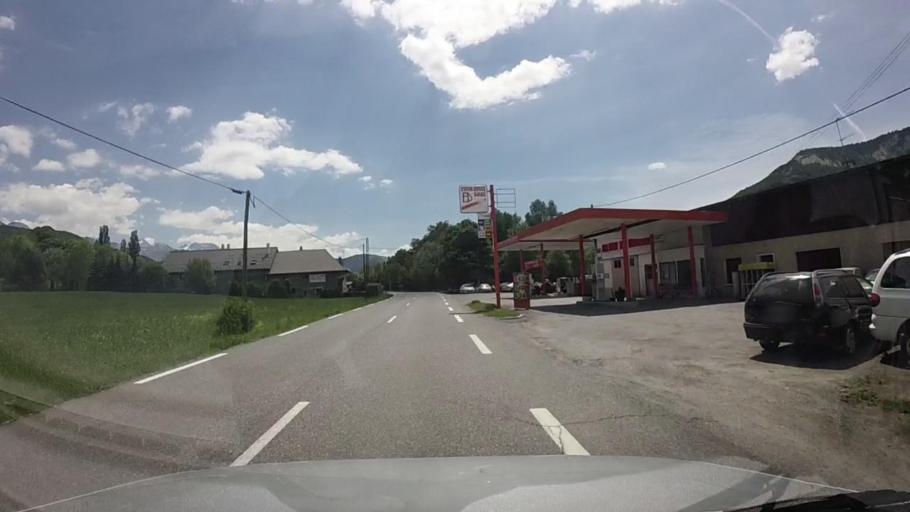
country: FR
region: Provence-Alpes-Cote d'Azur
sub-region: Departement des Alpes-de-Haute-Provence
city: Seyne-les-Alpes
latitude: 44.3674
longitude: 6.3192
